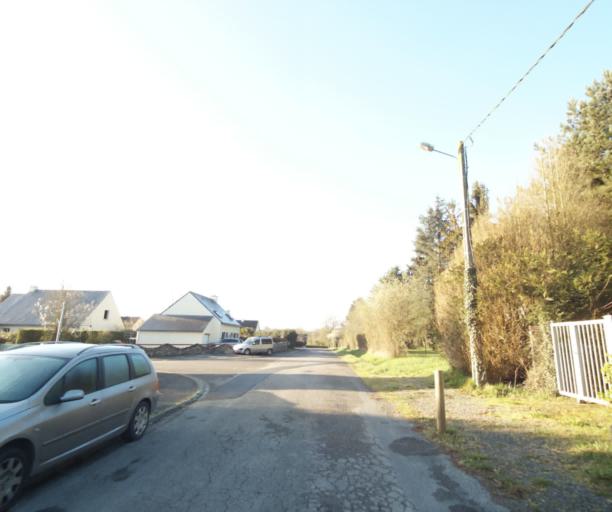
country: FR
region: Pays de la Loire
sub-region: Departement de la Loire-Atlantique
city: Bouvron
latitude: 47.4152
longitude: -1.8433
